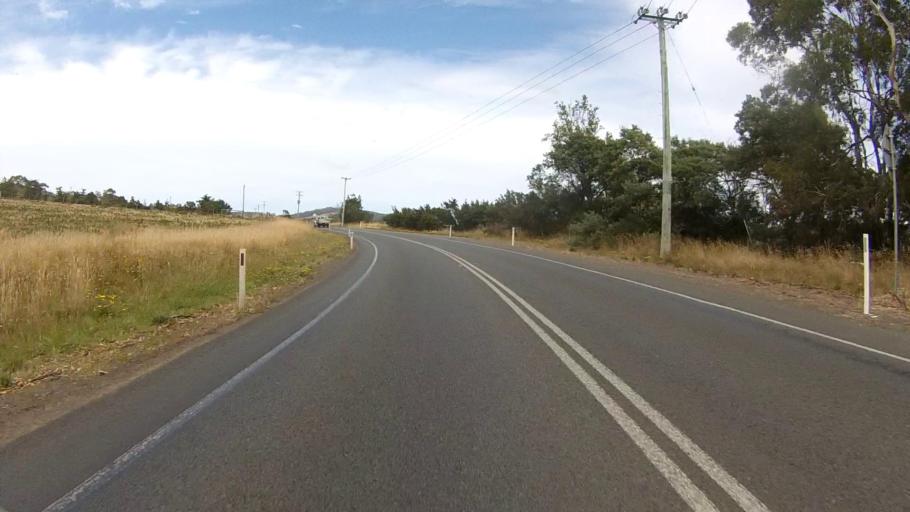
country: AU
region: Tasmania
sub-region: Clarence
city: Sandford
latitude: -42.9300
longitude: 147.4911
